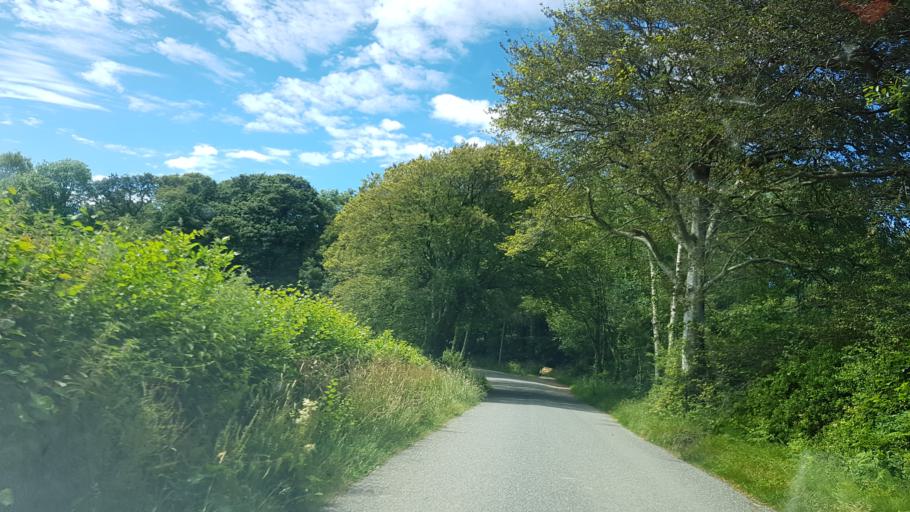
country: GB
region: Wales
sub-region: Pembrokeshire
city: Haverfordwest
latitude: 51.8202
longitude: -4.9392
